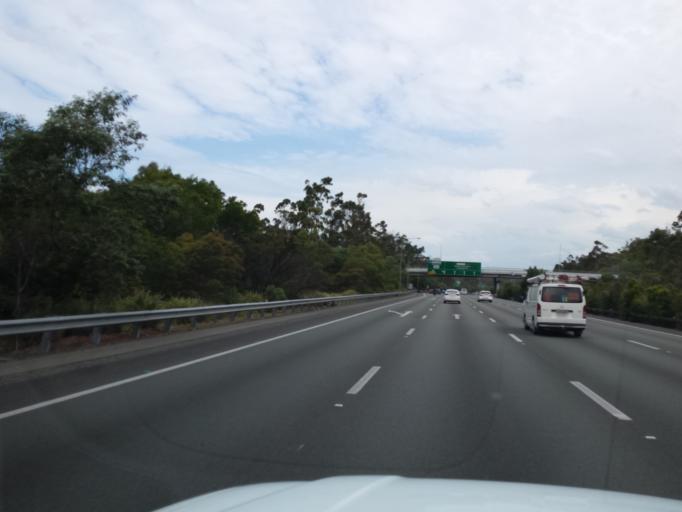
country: AU
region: Queensland
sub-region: Gold Coast
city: Nerang
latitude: -27.9489
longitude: 153.3415
